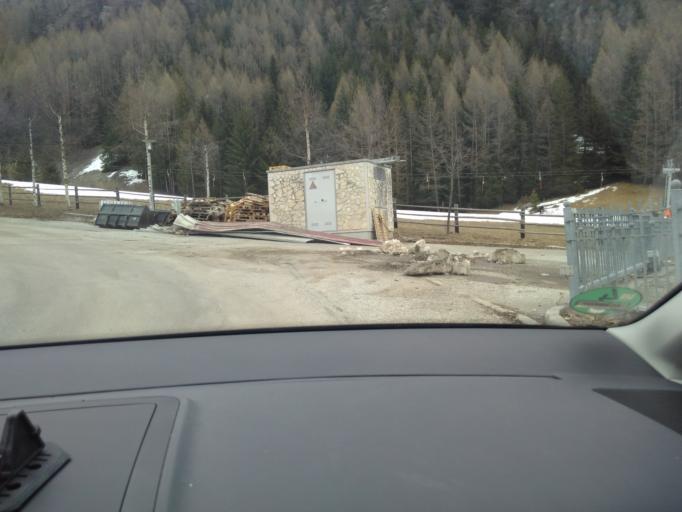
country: IT
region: Trentino-Alto Adige
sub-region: Bolzano
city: Fortezza
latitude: 46.8418
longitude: 11.6294
